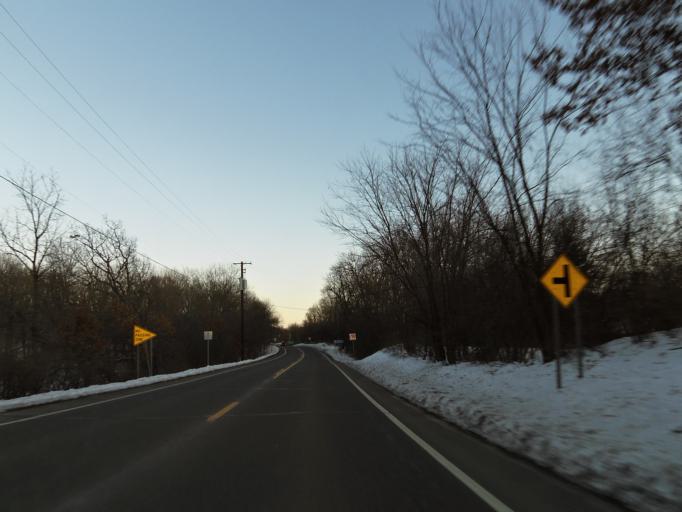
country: US
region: Minnesota
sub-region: Washington County
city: Dellwood
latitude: 45.0951
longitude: -92.9730
